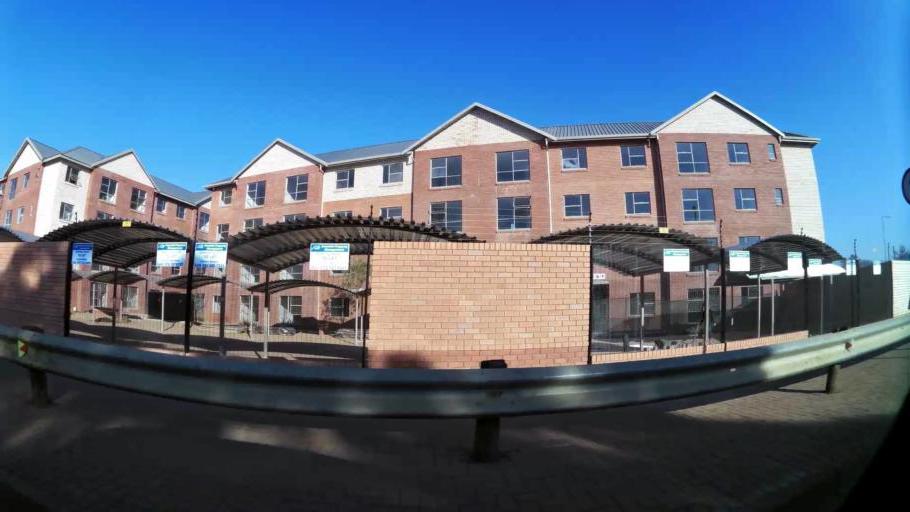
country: ZA
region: Gauteng
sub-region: City of Tshwane Metropolitan Municipality
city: Pretoria
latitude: -25.7142
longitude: 28.1843
